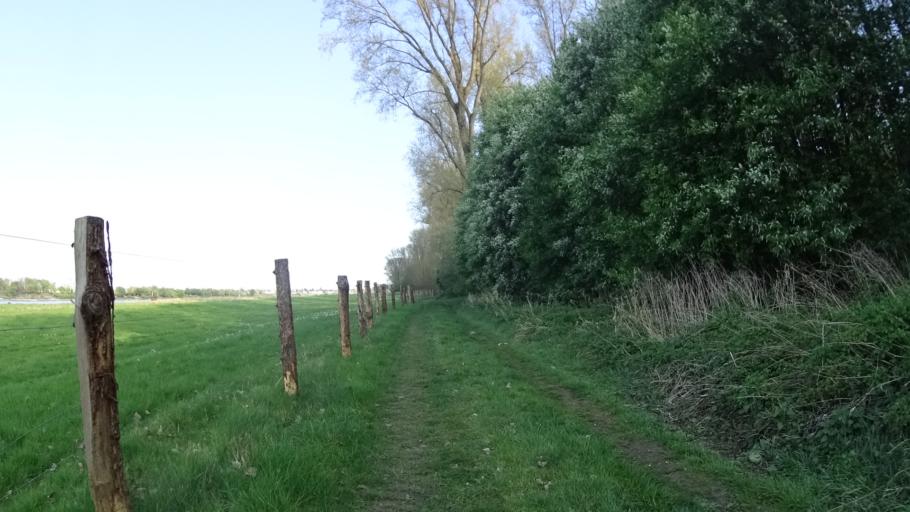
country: DE
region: North Rhine-Westphalia
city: Monheim am Rhein
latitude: 51.0666
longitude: 6.8825
